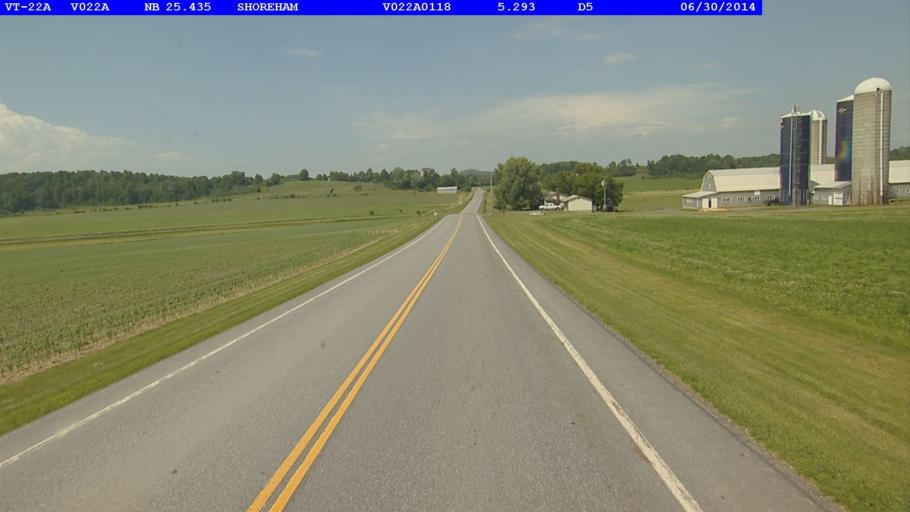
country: US
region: New York
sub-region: Essex County
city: Ticonderoga
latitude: 43.9253
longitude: -73.3109
